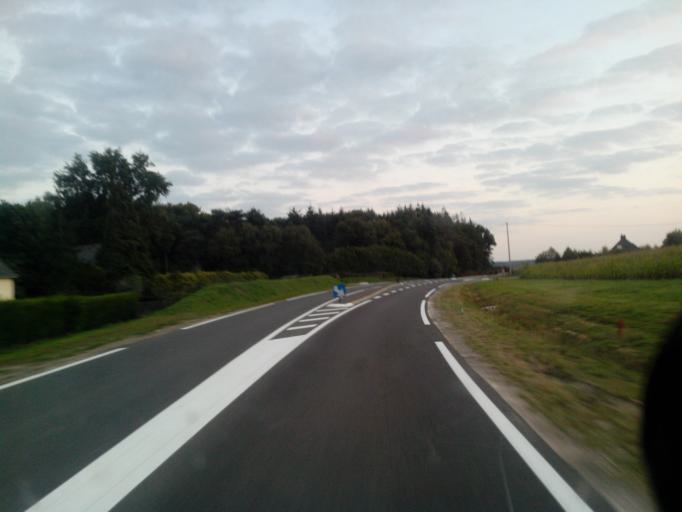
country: FR
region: Brittany
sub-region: Departement d'Ille-et-Vilaine
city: Bedee
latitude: 48.1608
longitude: -1.9454
